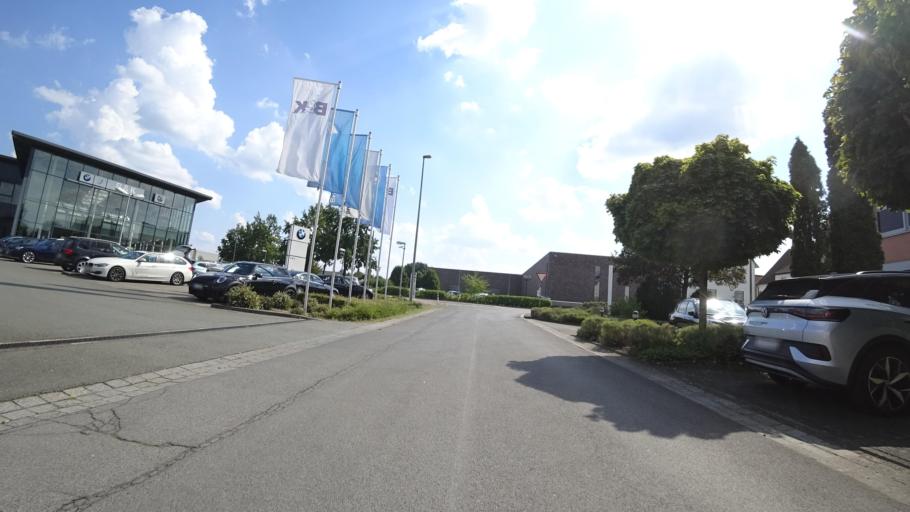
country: DE
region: North Rhine-Westphalia
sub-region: Regierungsbezirk Detmold
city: Guetersloh
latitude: 51.9193
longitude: 8.4094
